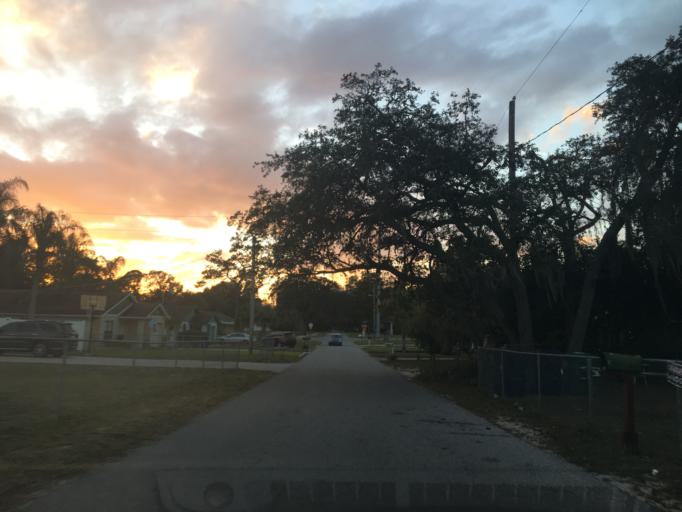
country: US
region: Florida
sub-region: Hillsborough County
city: University
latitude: 28.0377
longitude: -82.4295
